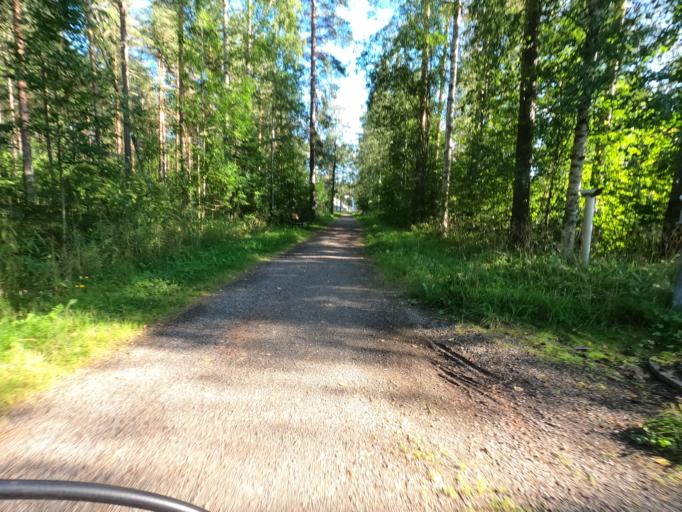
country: FI
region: North Karelia
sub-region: Joensuu
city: Joensuu
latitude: 62.6130
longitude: 29.7587
